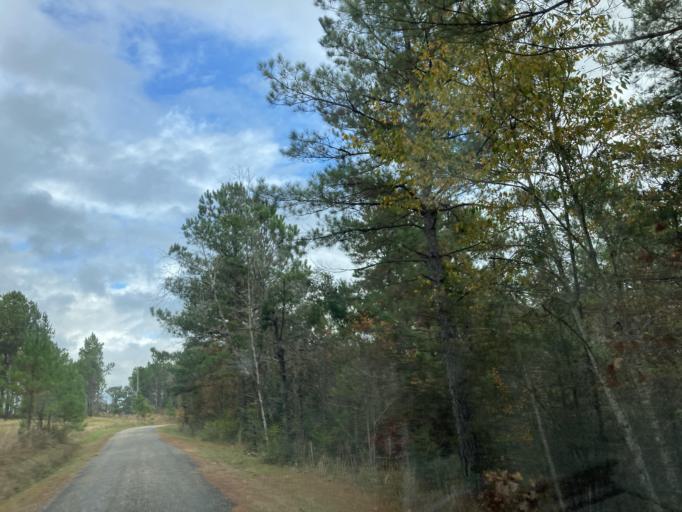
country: US
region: Mississippi
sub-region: Lamar County
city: Purvis
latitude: 31.1509
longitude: -89.5539
